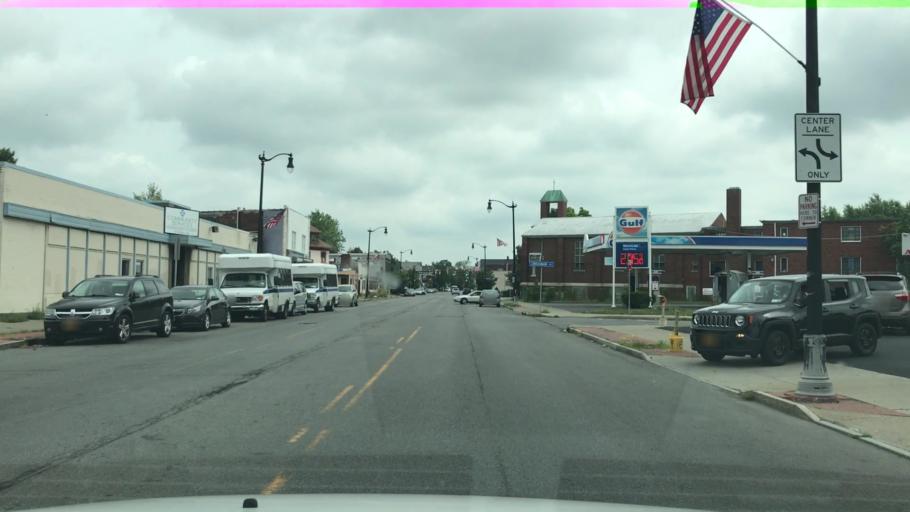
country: US
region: New York
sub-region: Erie County
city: Sloan
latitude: 42.9169
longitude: -78.8031
